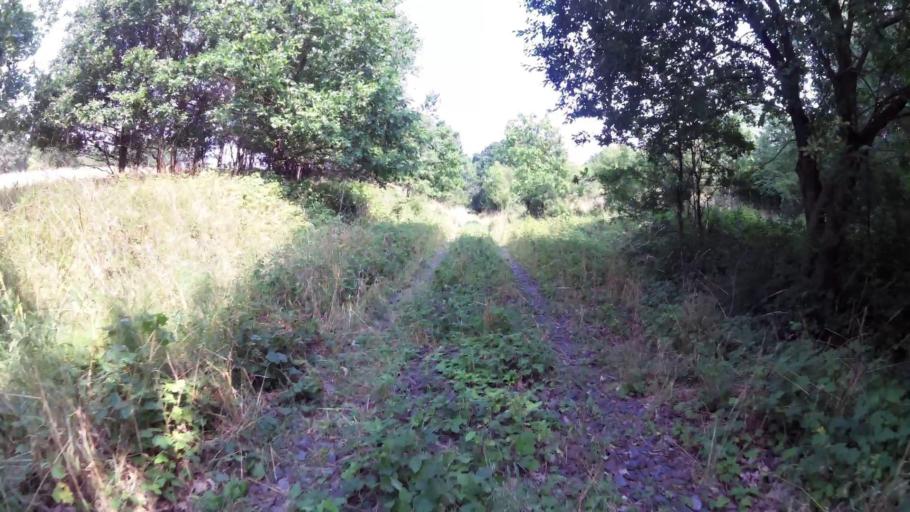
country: PL
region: West Pomeranian Voivodeship
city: Trzcinsko Zdroj
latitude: 52.9170
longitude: 14.5499
